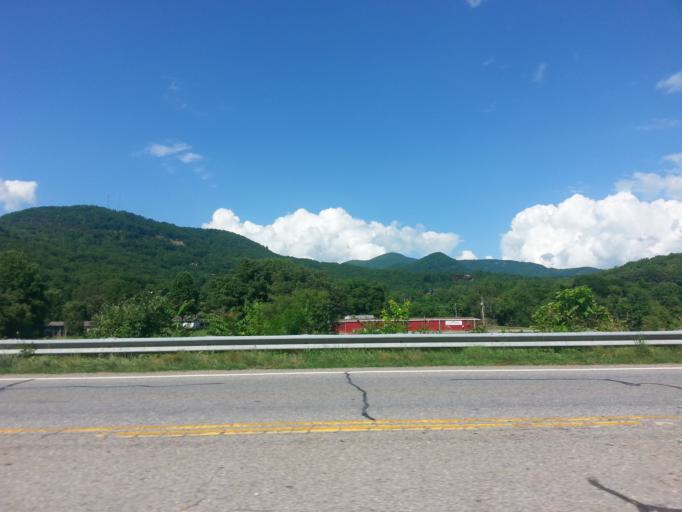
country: US
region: Georgia
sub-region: Towns County
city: Hiawassee
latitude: 34.9388
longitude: -83.7405
